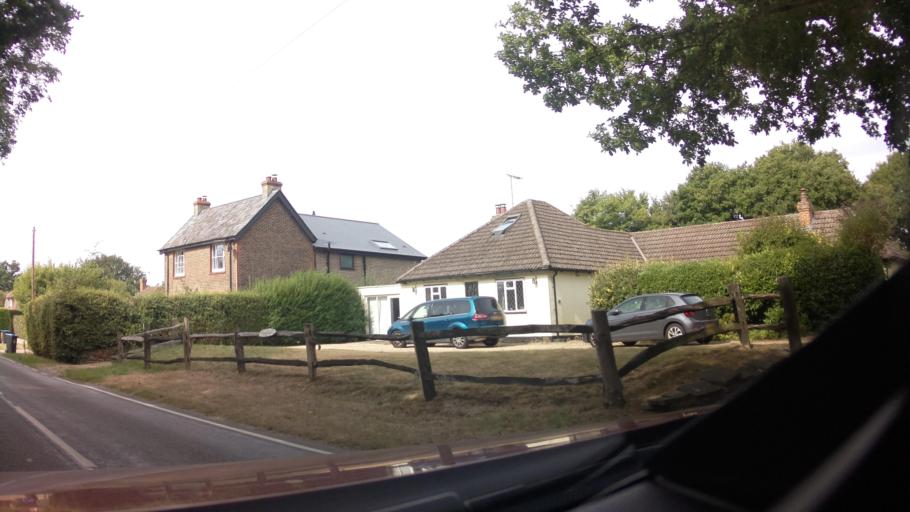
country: GB
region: England
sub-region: Surrey
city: Lingfield
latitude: 51.1912
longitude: -0.0674
